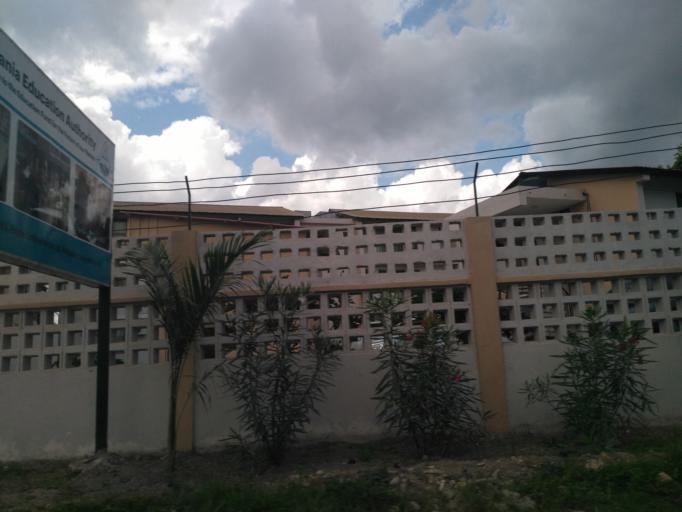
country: TZ
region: Dar es Salaam
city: Magomeni
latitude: -6.7563
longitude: 39.2392
